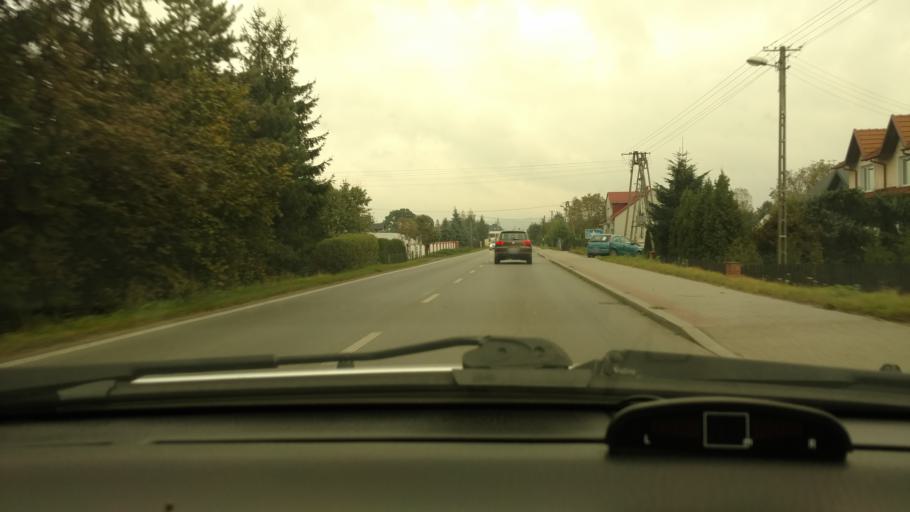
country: PL
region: Lesser Poland Voivodeship
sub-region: Powiat nowosadecki
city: Chelmiec
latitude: 49.6154
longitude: 20.6640
